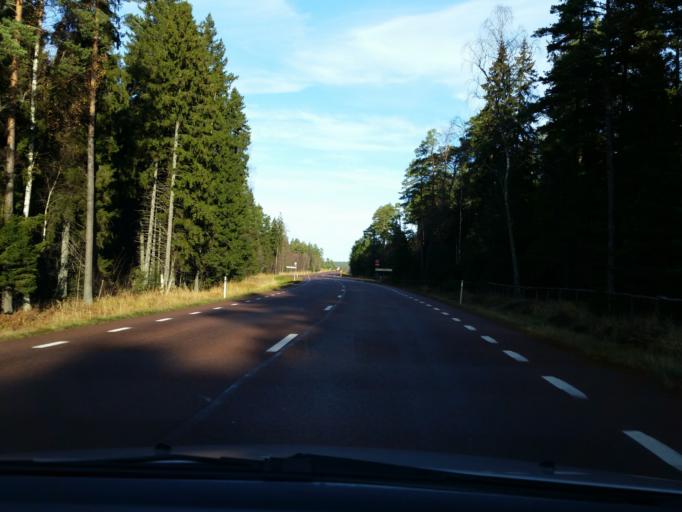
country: AX
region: Alands landsbygd
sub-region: Finstroem
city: Finstroem
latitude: 60.2815
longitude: 19.9528
